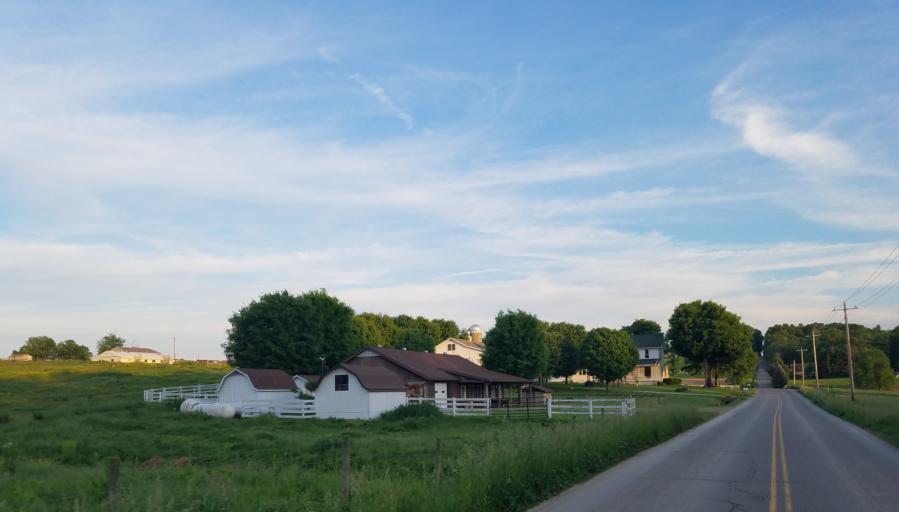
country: US
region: Ohio
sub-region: Knox County
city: Danville
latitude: 40.5280
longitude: -82.3611
